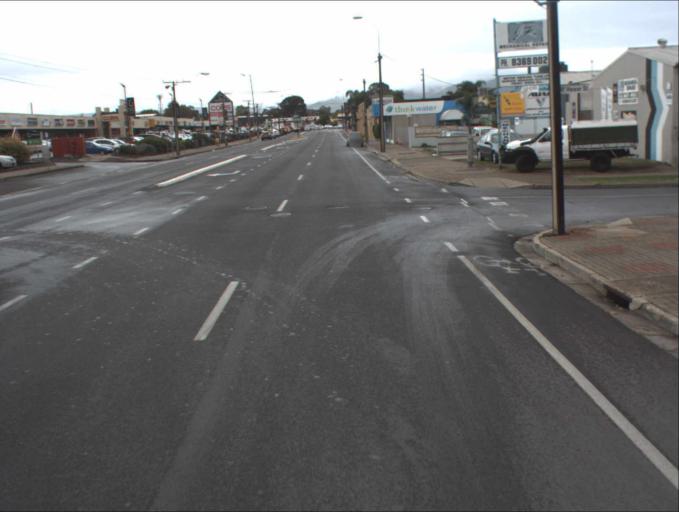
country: AU
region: South Australia
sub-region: Port Adelaide Enfield
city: Klemzig
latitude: -34.8713
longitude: 138.6339
